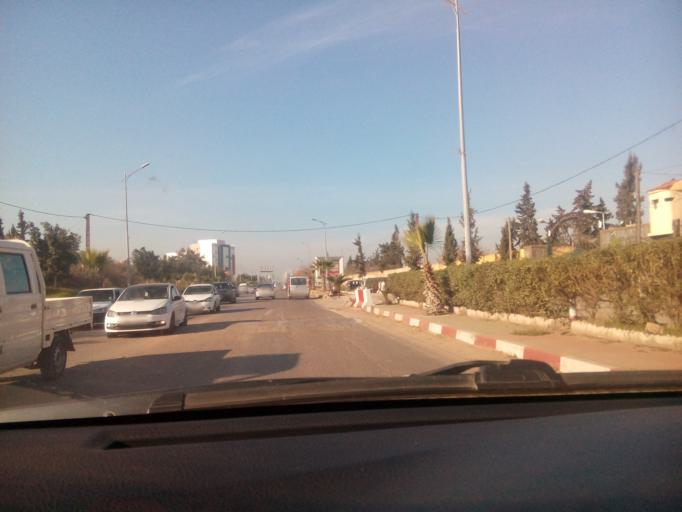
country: DZ
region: Oran
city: Es Senia
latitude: 35.6599
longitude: -0.6194
